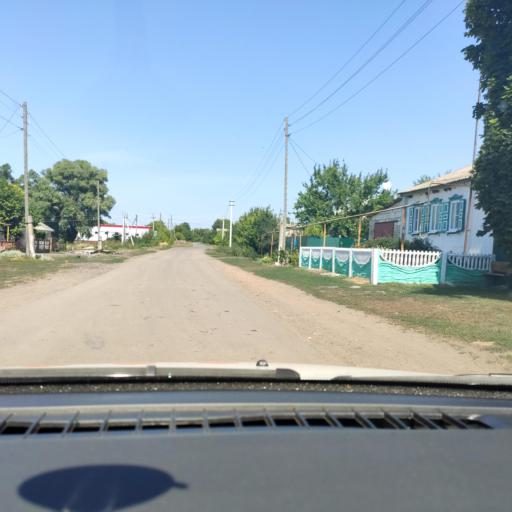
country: RU
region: Voronezj
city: Ol'khovatka
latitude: 50.5705
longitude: 39.2622
